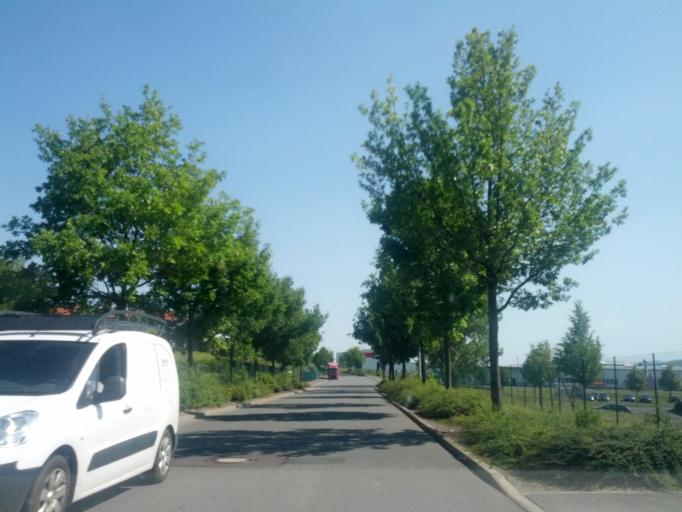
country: DE
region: Thuringia
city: Haina
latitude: 51.0021
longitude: 10.4453
